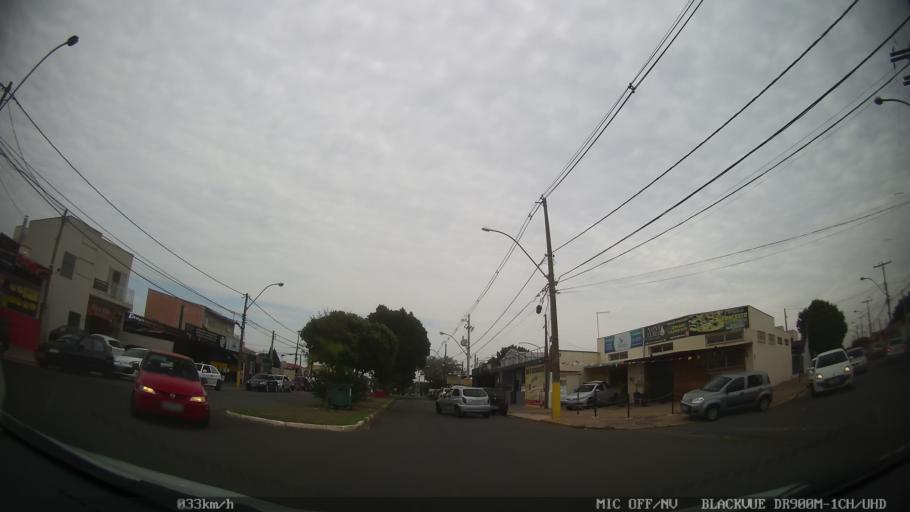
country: BR
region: Sao Paulo
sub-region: Paulinia
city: Paulinia
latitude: -22.7335
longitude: -47.1783
